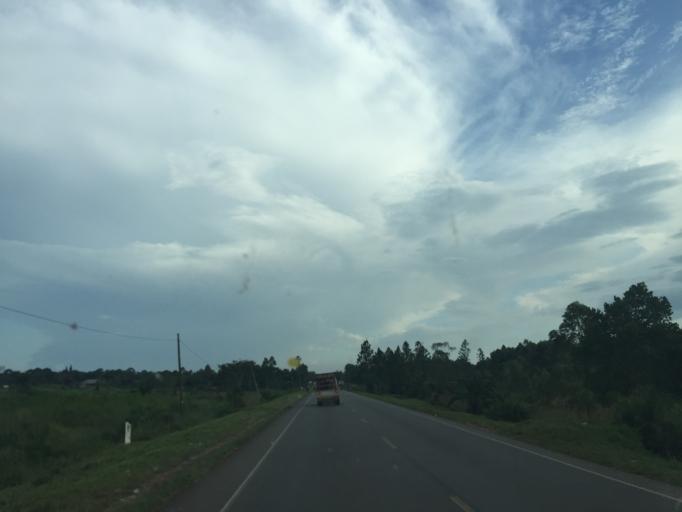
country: UG
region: Central Region
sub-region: Luwero District
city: Luwero
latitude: 0.8677
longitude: 32.4853
